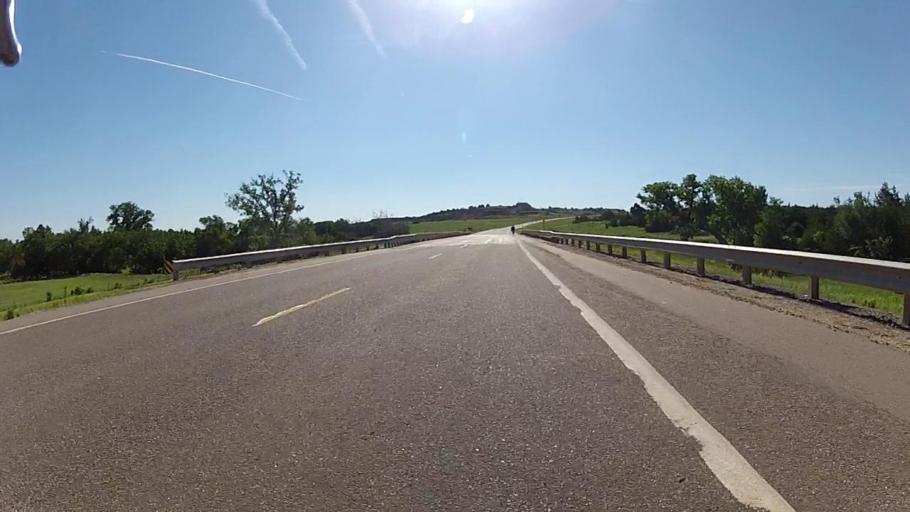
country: US
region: Kansas
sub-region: Barber County
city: Medicine Lodge
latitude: 37.2824
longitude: -98.7570
